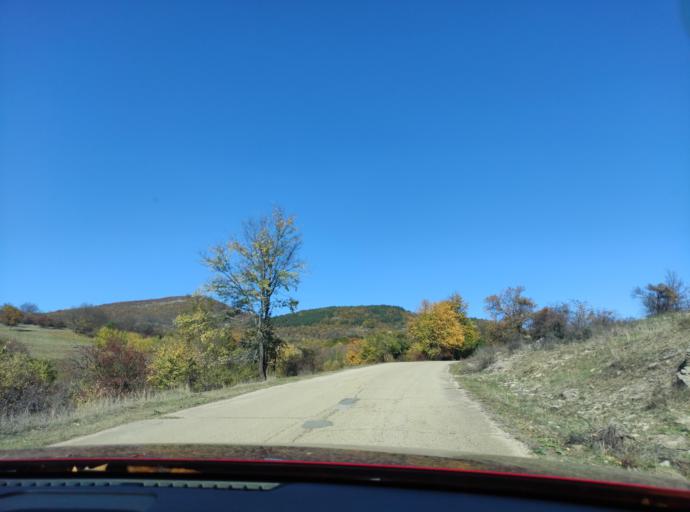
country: BG
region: Montana
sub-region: Obshtina Chiprovtsi
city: Chiprovtsi
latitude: 43.4488
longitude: 23.0463
